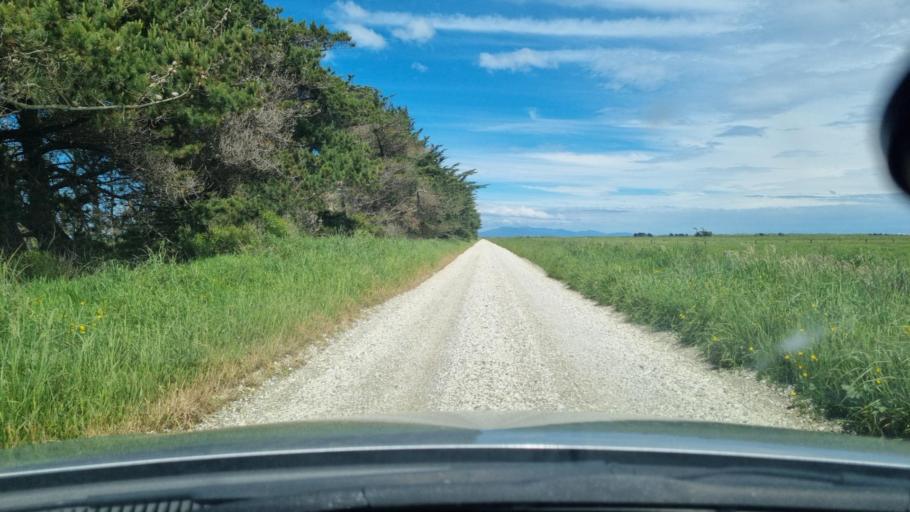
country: NZ
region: Southland
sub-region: Invercargill City
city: Invercargill
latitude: -46.3838
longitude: 168.2666
